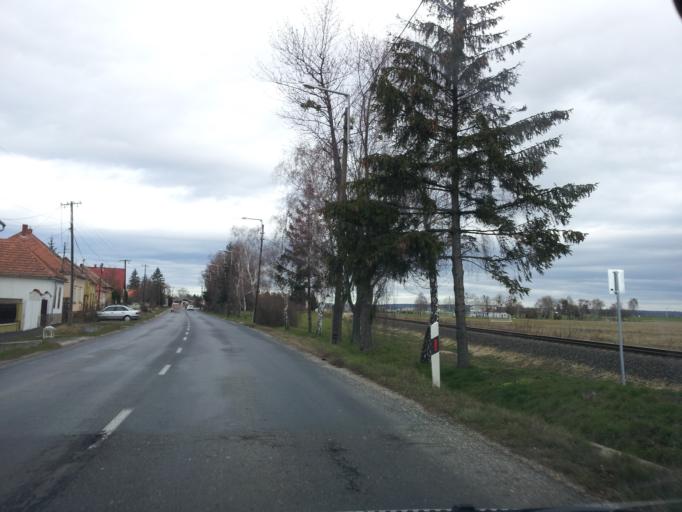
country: HU
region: Vas
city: Gencsapati
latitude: 47.3246
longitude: 16.5858
